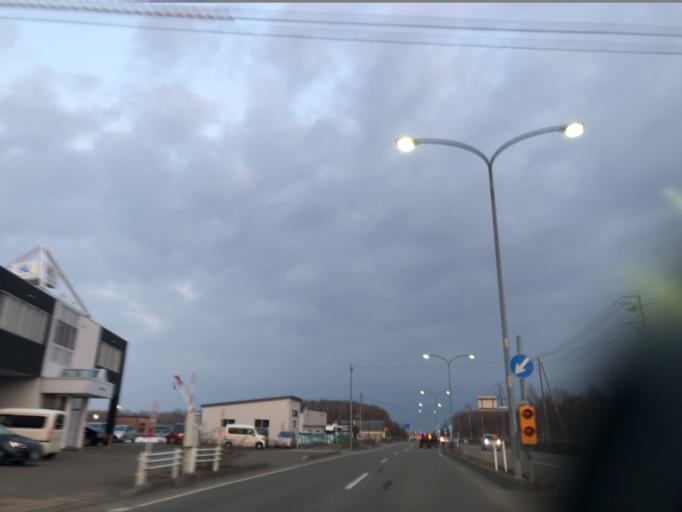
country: JP
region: Hokkaido
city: Chitose
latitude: 42.8209
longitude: 141.6742
